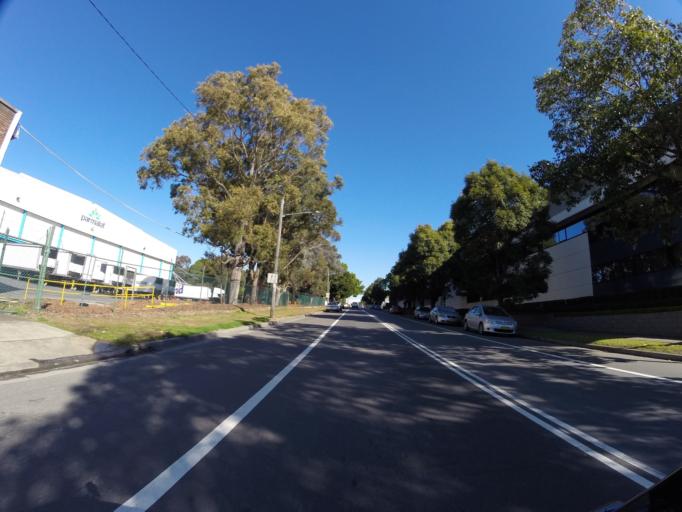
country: AU
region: New South Wales
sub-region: Auburn
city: Lidcombe
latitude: -33.8577
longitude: 151.0596
